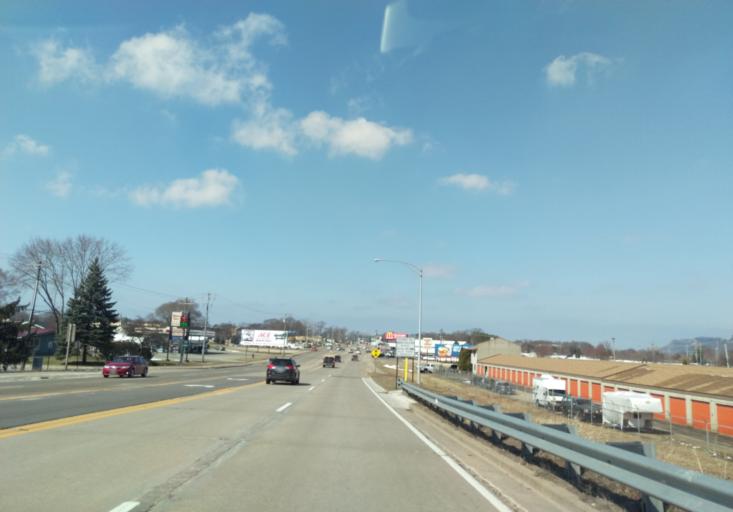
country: US
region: Wisconsin
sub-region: La Crosse County
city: La Crosse
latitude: 43.7631
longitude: -91.2085
